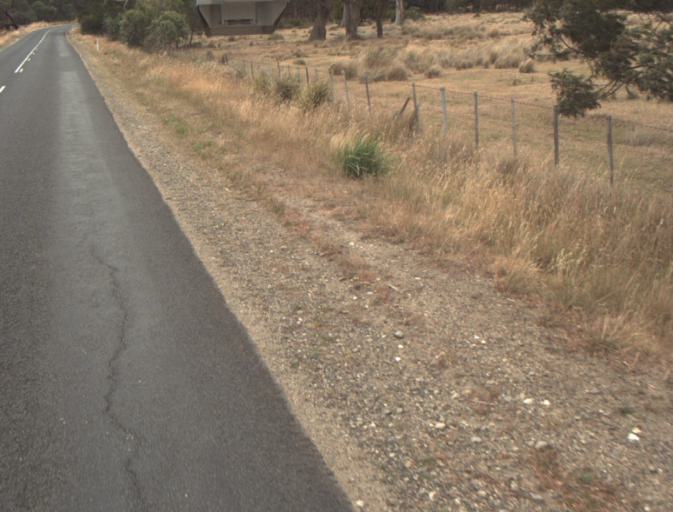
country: AU
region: Tasmania
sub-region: Northern Midlands
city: Evandale
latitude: -41.5120
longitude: 147.3107
